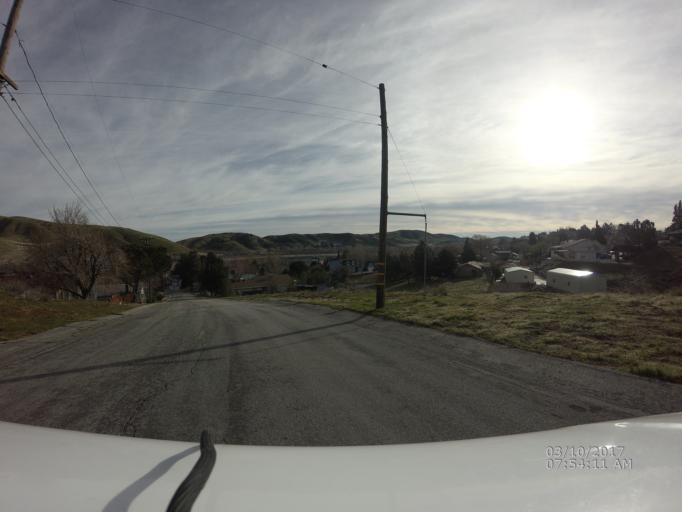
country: US
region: California
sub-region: Los Angeles County
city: Green Valley
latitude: 34.6627
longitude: -118.4029
